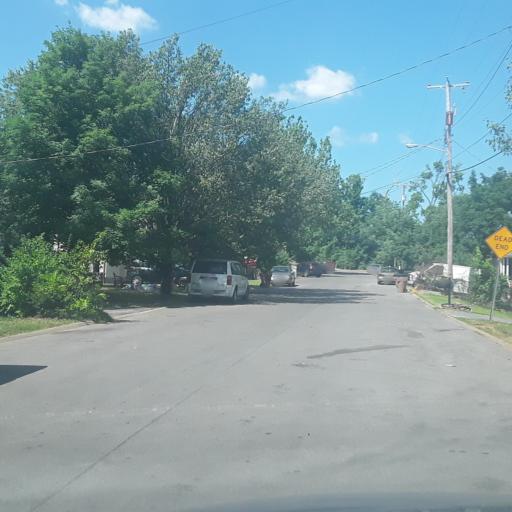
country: US
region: Tennessee
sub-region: Williamson County
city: Brentwood Estates
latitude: 36.0421
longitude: -86.7063
